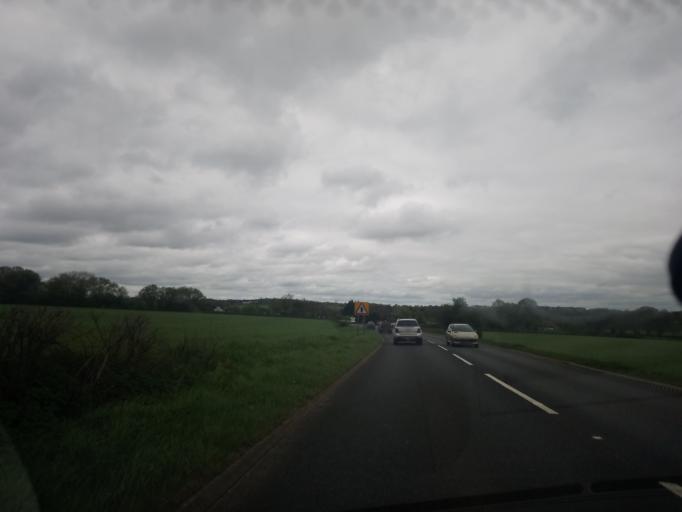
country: GB
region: England
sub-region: Telford and Wrekin
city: Chetwynd
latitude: 52.8239
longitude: -2.4528
